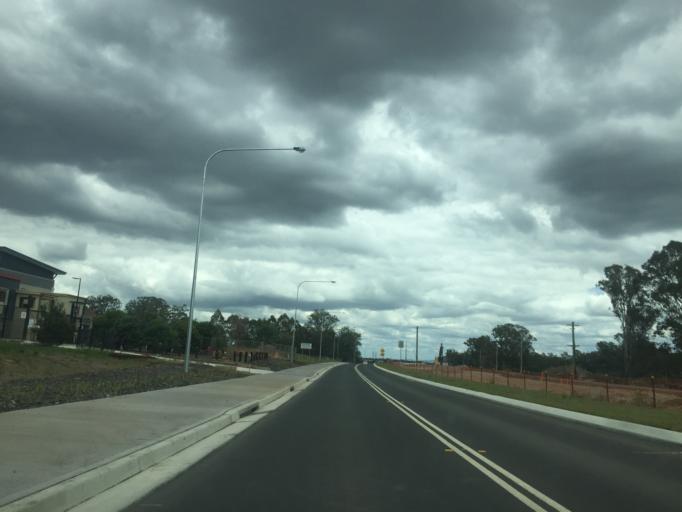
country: AU
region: New South Wales
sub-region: Blacktown
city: Riverstone
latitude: -33.6993
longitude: 150.8787
